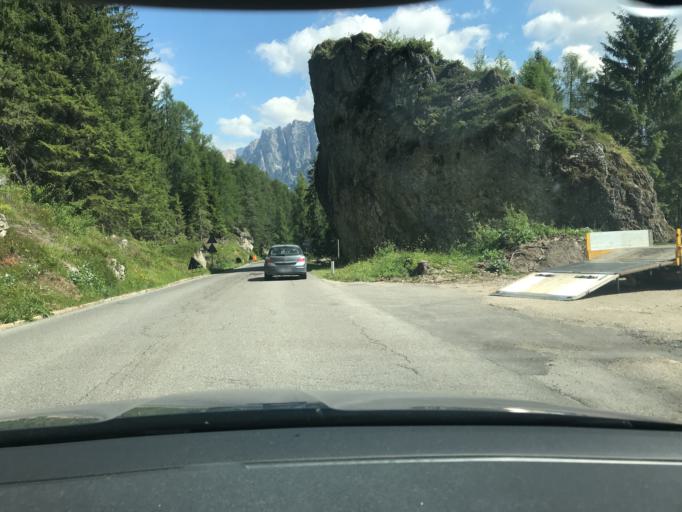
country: IT
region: Veneto
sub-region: Provincia di Belluno
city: Cortina d'Ampezzo
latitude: 46.5237
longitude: 12.1199
